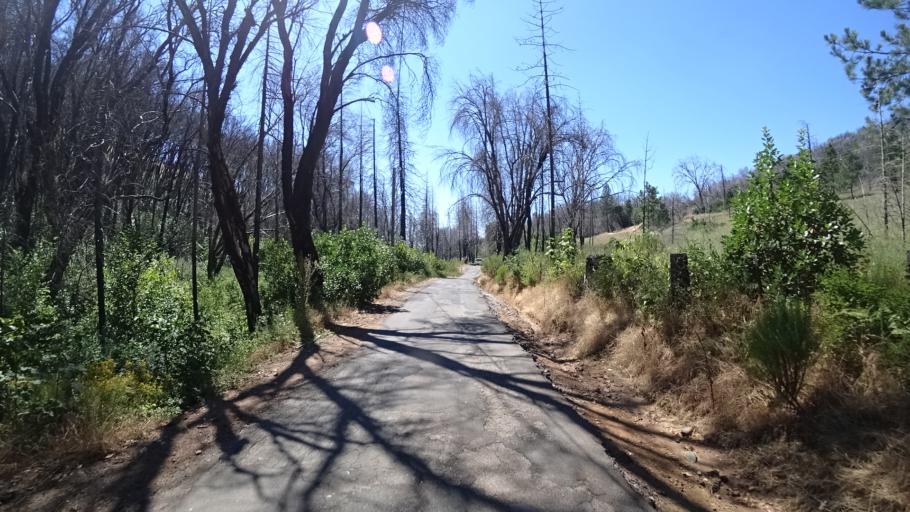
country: US
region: California
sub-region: Calaveras County
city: Mountain Ranch
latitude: 38.2828
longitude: -120.5614
